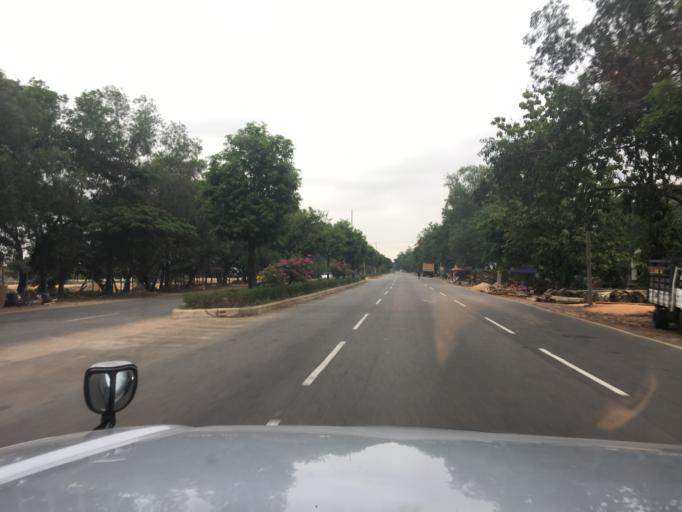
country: MM
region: Bago
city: Bago
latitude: 17.2248
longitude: 96.4485
